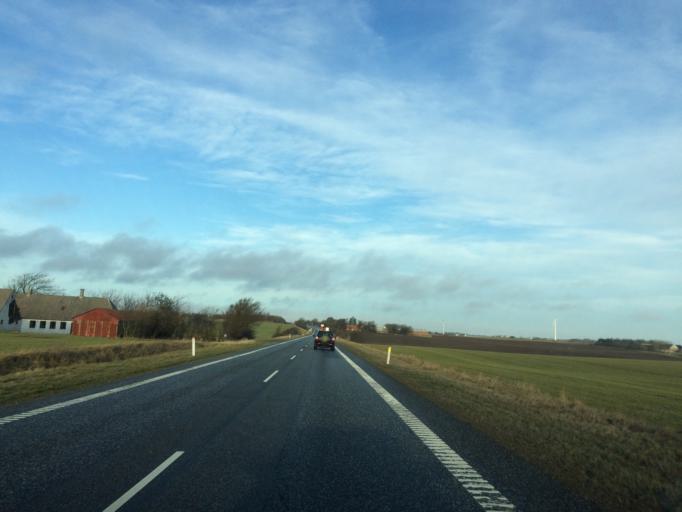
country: DK
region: North Denmark
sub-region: Thisted Kommune
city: Thisted
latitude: 56.8775
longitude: 8.5910
